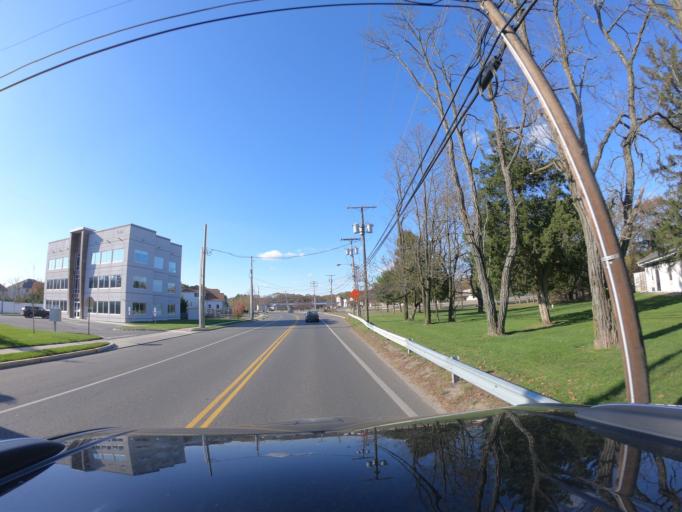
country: US
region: New Jersey
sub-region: Monmouth County
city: Ramtown
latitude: 40.1029
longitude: -74.1737
